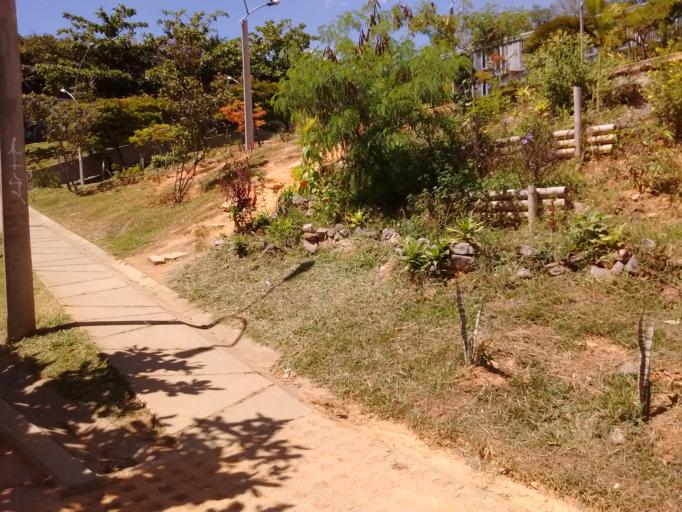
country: CO
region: Antioquia
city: Medellin
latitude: 6.2552
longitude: -75.6133
